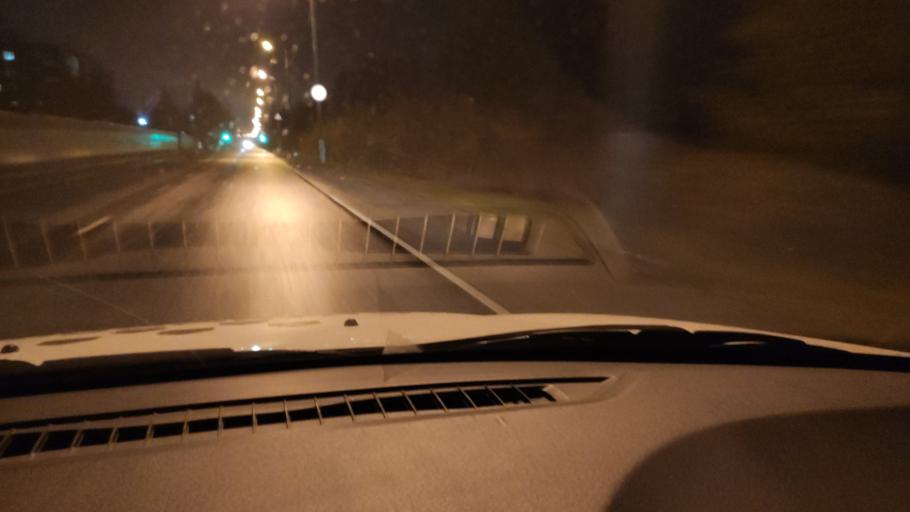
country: RU
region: Perm
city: Kondratovo
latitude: 57.9791
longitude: 56.1306
